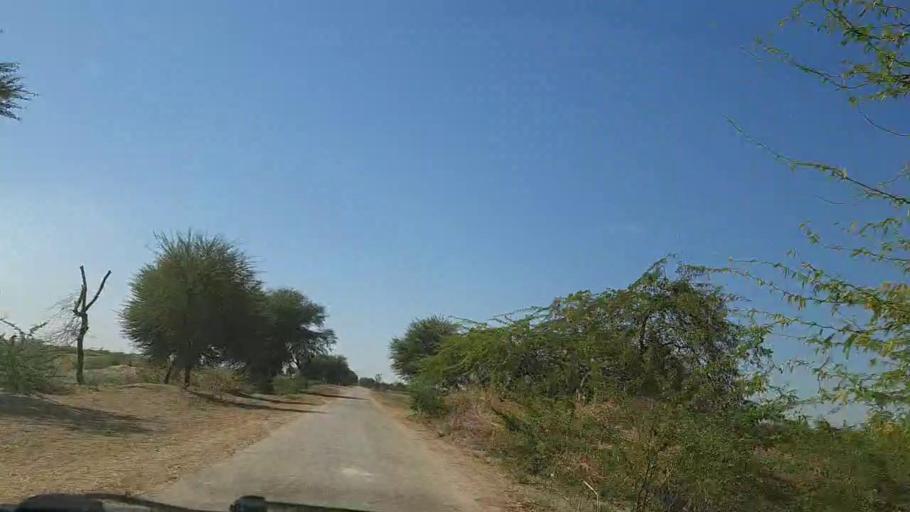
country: PK
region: Sindh
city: Dhoro Naro
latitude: 25.5228
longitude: 69.5233
